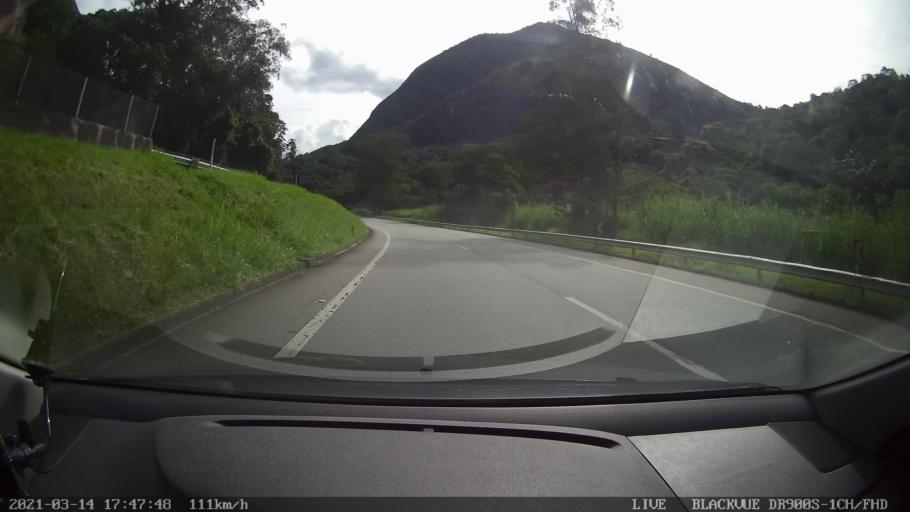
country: BR
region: Rio de Janeiro
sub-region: Petropolis
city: Petropolis
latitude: -22.4378
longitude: -43.1839
